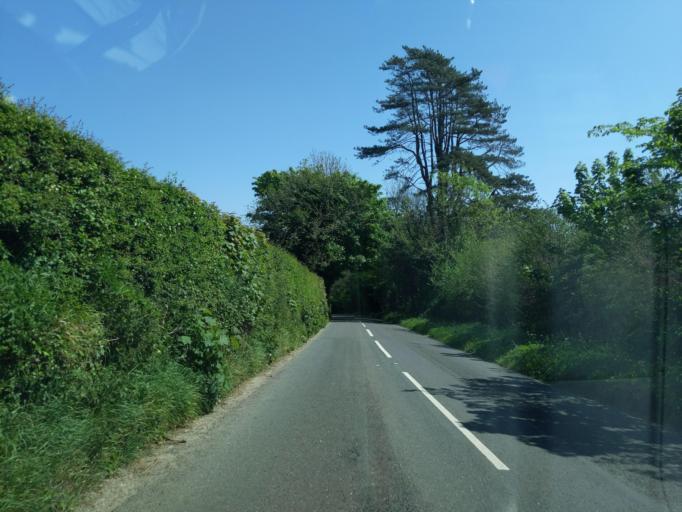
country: GB
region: England
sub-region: Cornwall
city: Pillaton
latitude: 50.3994
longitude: -4.3227
